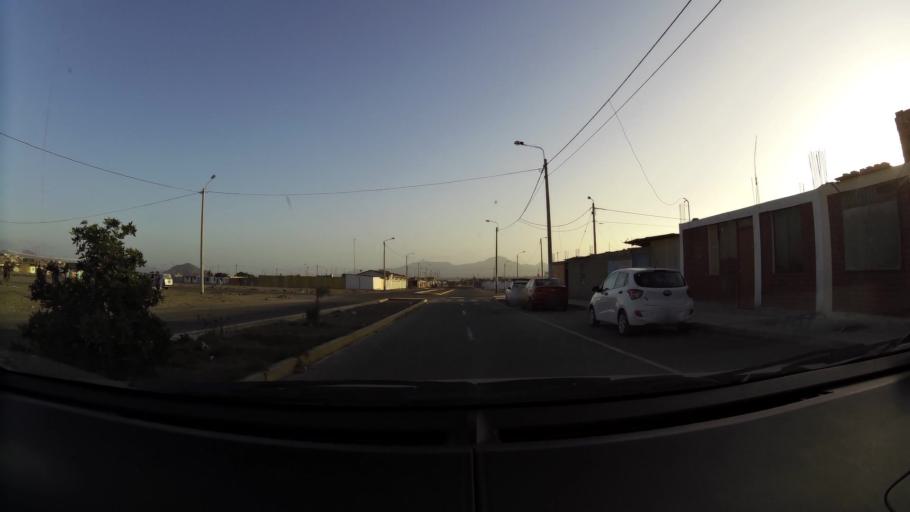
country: PE
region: Ancash
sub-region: Provincia de Santa
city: Buenos Aires
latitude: -9.1463
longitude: -78.5008
